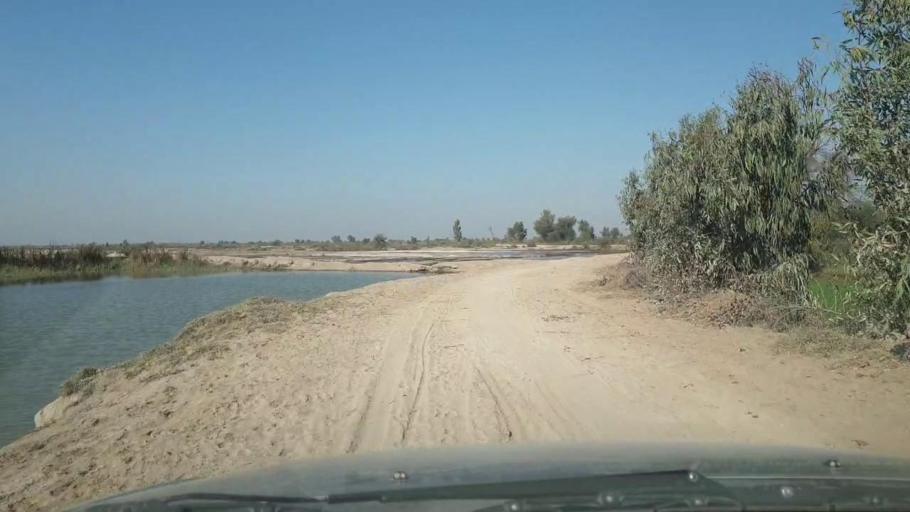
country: PK
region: Sindh
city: Adilpur
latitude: 27.8936
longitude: 69.2553
